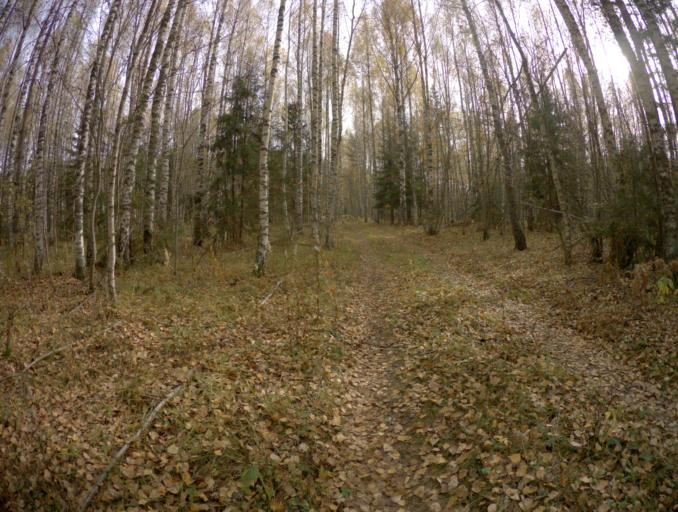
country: RU
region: Vladimir
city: Vorsha
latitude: 55.9577
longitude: 40.1435
